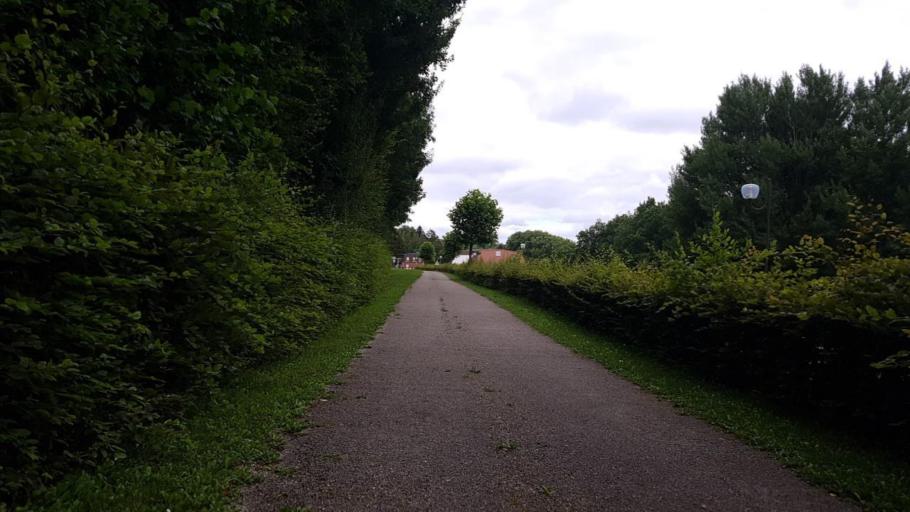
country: FR
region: Picardie
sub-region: Departement de l'Aisne
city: Hirson
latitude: 49.9110
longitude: 4.0617
